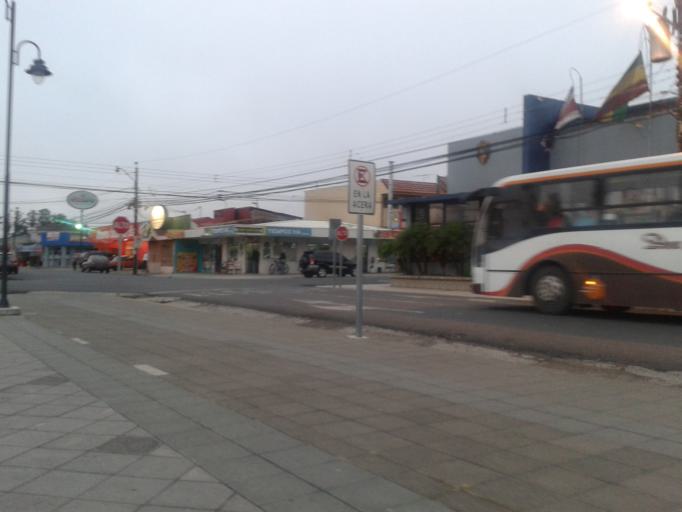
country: CR
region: Cartago
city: Cartago
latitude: 9.8449
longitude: -83.9388
